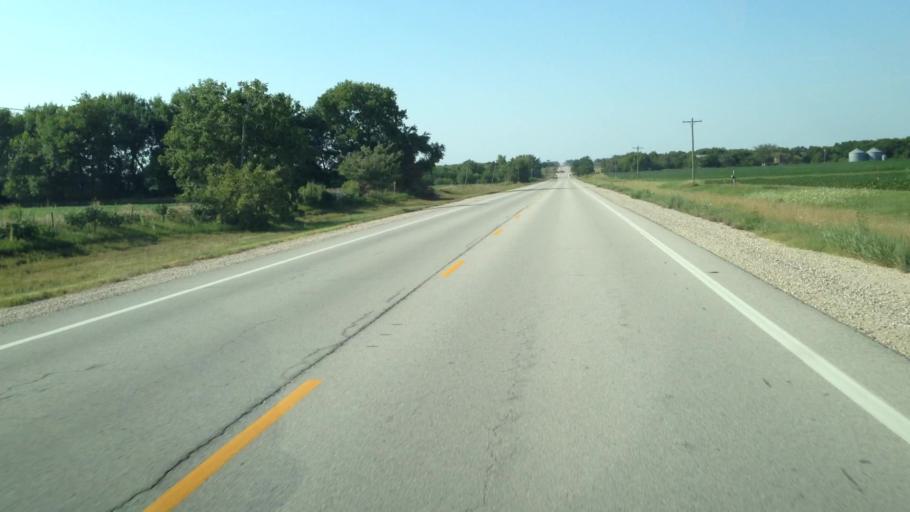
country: US
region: Kansas
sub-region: Anderson County
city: Garnett
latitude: 38.1024
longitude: -95.2429
